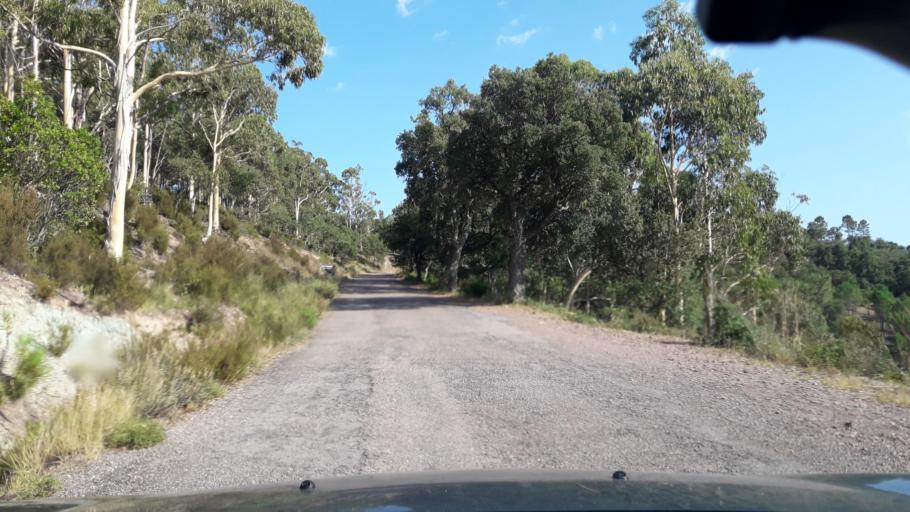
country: FR
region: Provence-Alpes-Cote d'Azur
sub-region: Departement du Var
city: Saint-Raphael
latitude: 43.4974
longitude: 6.8007
